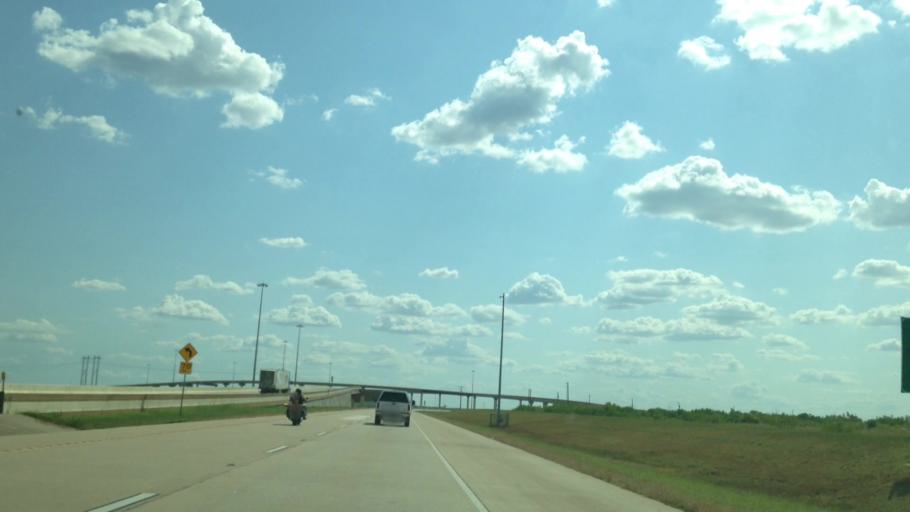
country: US
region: Texas
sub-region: Travis County
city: Onion Creek
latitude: 30.0882
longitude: -97.6861
